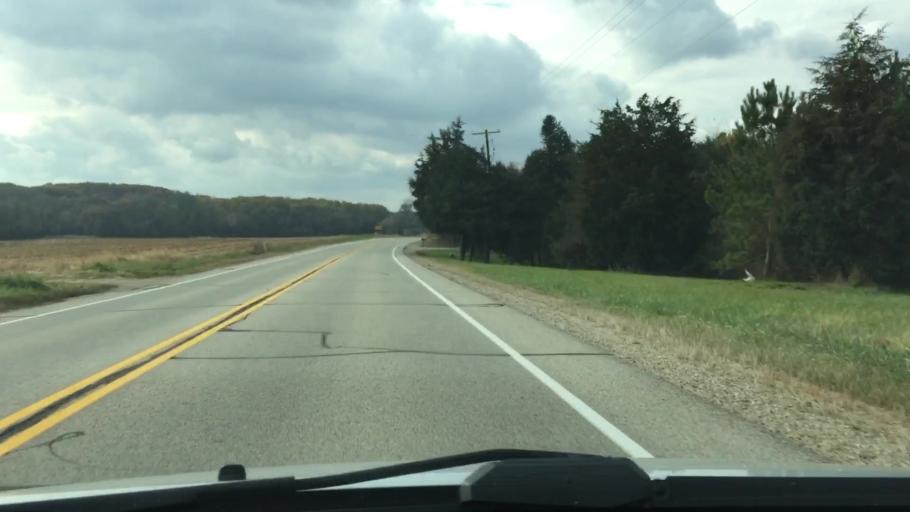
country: US
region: Wisconsin
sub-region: Waukesha County
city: Dousman
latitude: 42.9791
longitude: -88.4665
